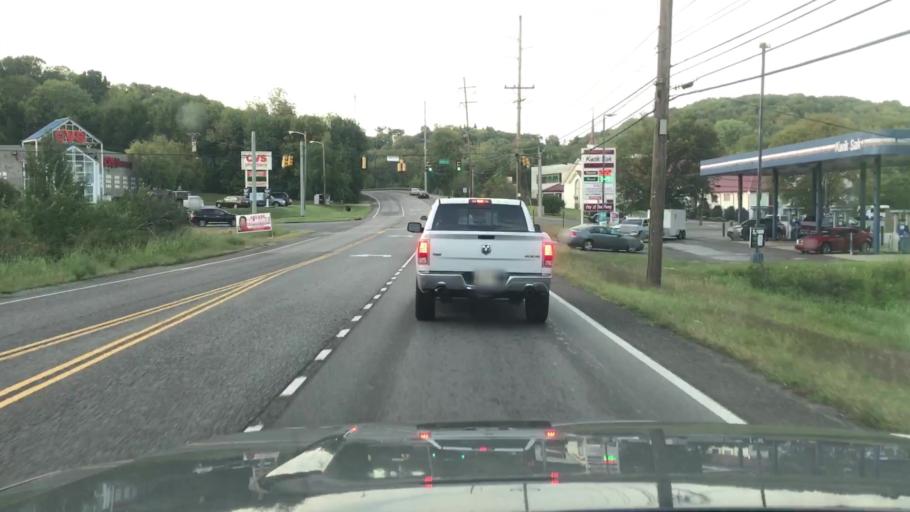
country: US
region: Tennessee
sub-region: Davidson County
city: Nashville
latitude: 36.2177
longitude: -86.8372
